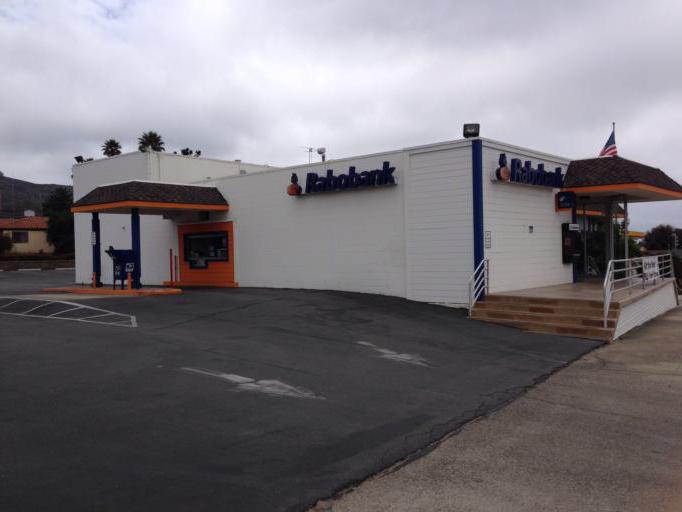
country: US
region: California
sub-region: San Luis Obispo County
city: Los Osos
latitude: 35.3110
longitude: -120.8324
